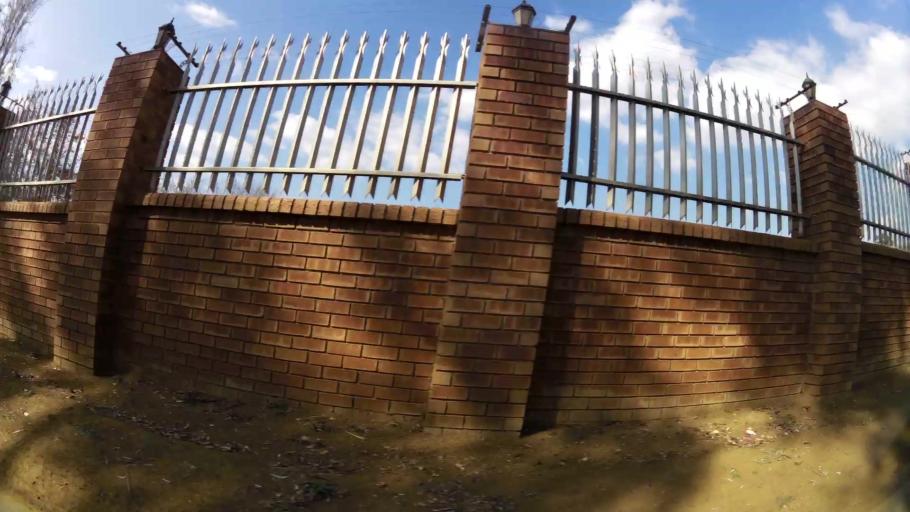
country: ZA
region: Gauteng
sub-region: City of Johannesburg Metropolitan Municipality
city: Modderfontein
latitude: -26.0907
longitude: 28.2601
